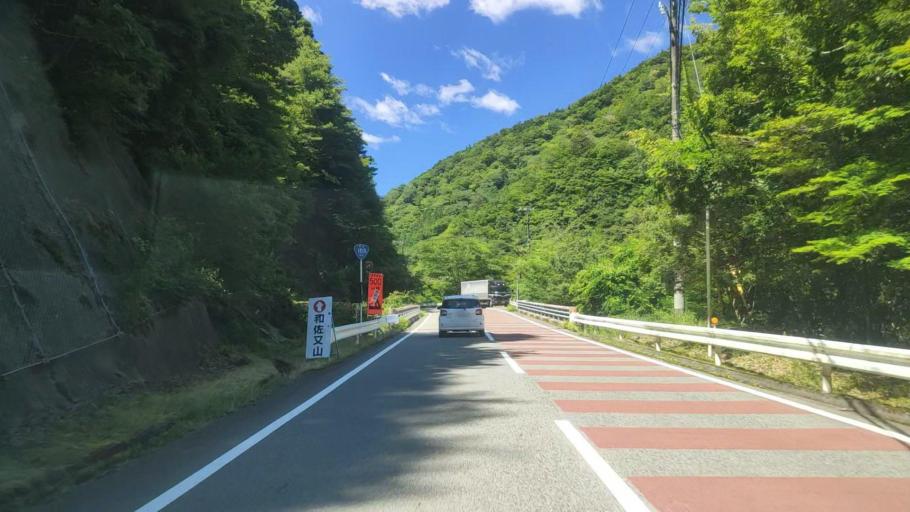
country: JP
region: Nara
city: Yoshino-cho
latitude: 34.2004
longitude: 135.9989
